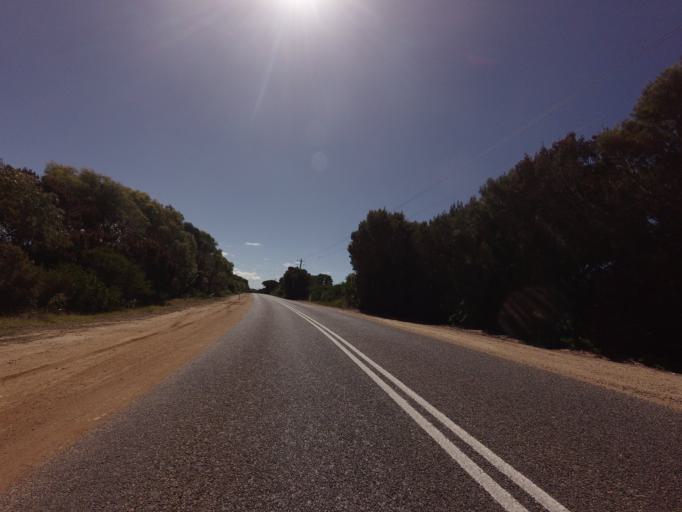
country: AU
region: Tasmania
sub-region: Break O'Day
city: St Helens
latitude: -41.8260
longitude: 148.2628
